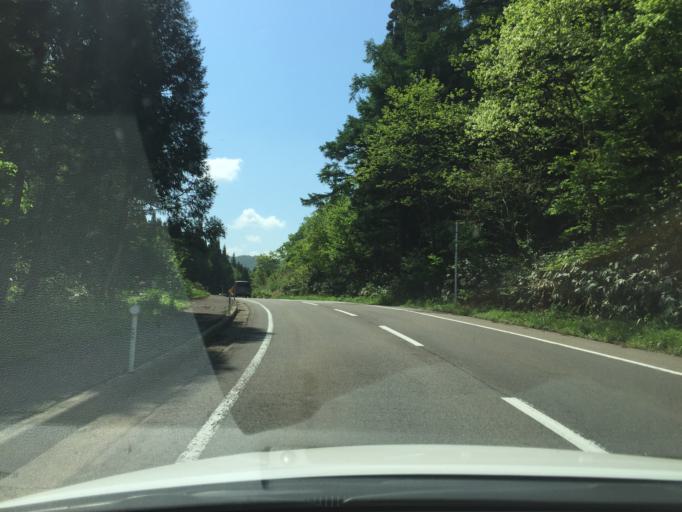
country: JP
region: Niigata
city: Kamo
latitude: 37.5843
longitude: 139.0920
